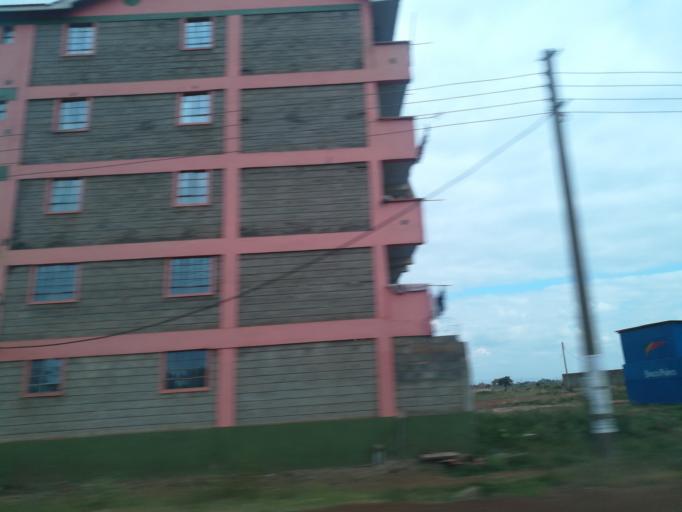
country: KE
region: Nairobi Area
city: Thika
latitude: -1.0973
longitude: 37.0265
